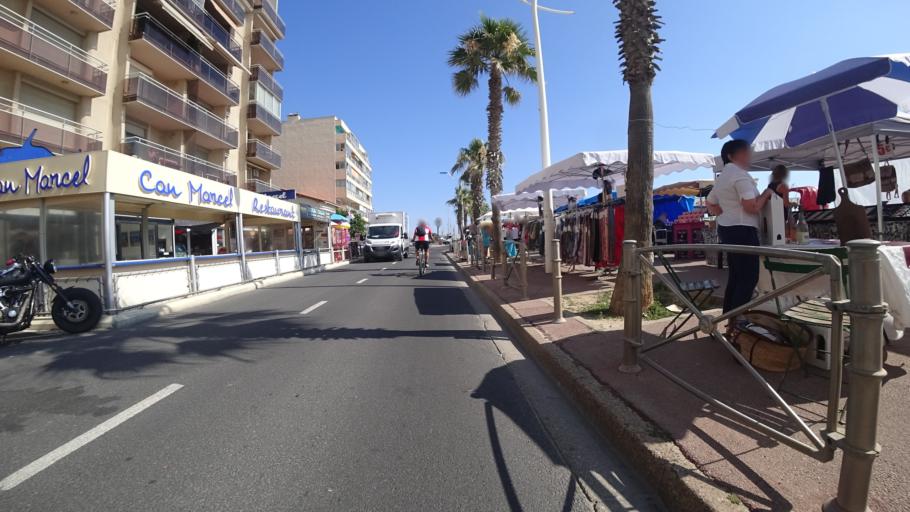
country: FR
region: Languedoc-Roussillon
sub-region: Departement des Pyrenees-Orientales
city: Canet-en-Roussillon
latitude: 42.7006
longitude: 3.0366
